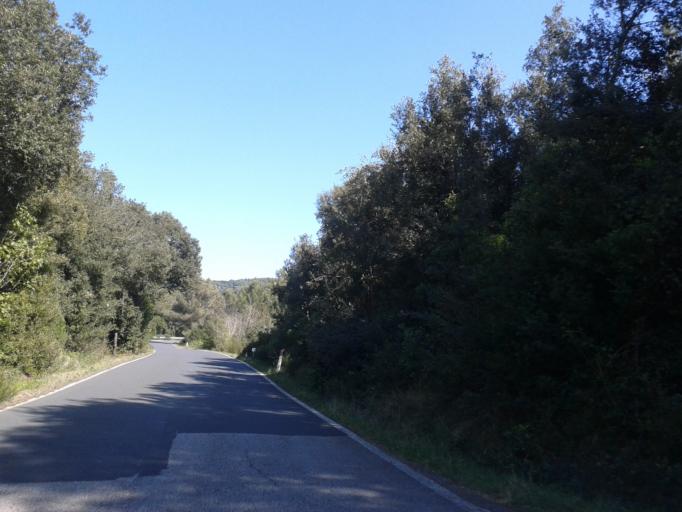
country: IT
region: Tuscany
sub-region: Provincia di Livorno
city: Quercianella
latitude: 43.4534
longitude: 10.3893
